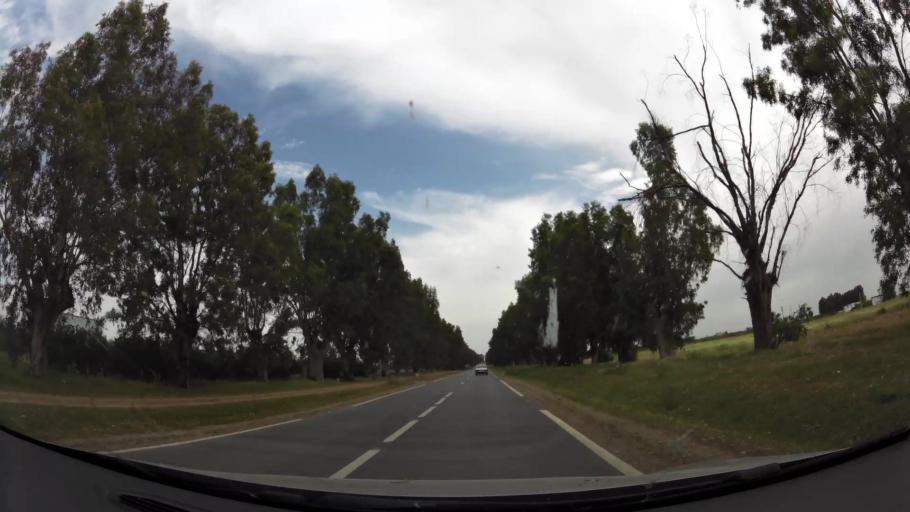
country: MA
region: Rabat-Sale-Zemmour-Zaer
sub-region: Khemisset
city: Tiflet
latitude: 33.8612
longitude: -6.2710
